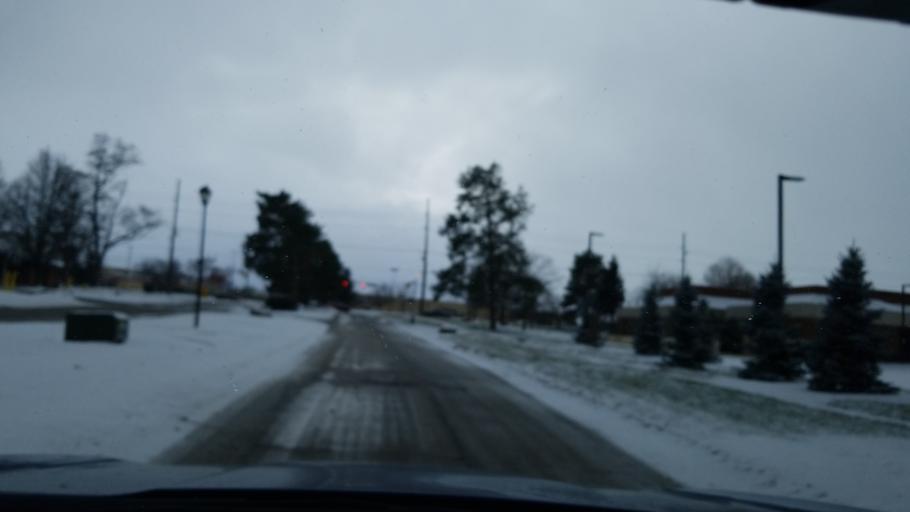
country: US
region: Ohio
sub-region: Cuyahoga County
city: Strongsville
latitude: 41.3143
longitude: -81.8220
